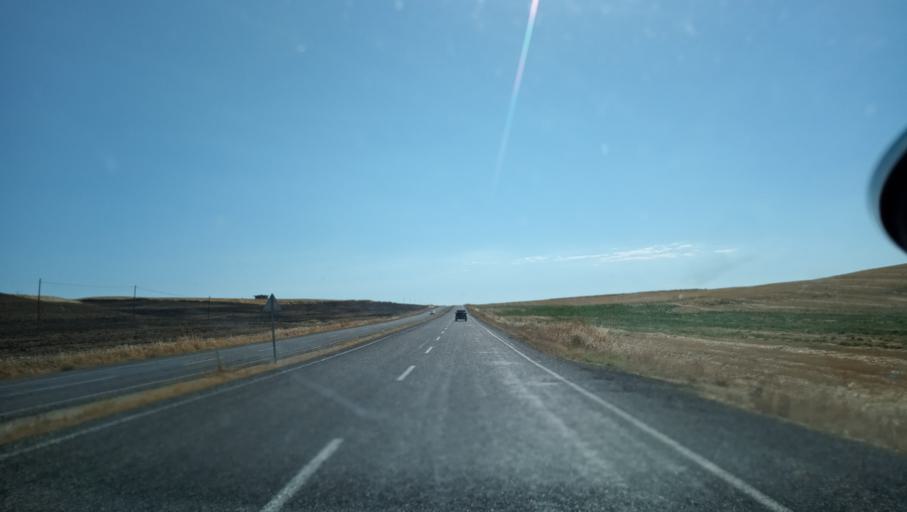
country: TR
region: Diyarbakir
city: Bagdere
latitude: 38.1286
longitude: 40.7858
